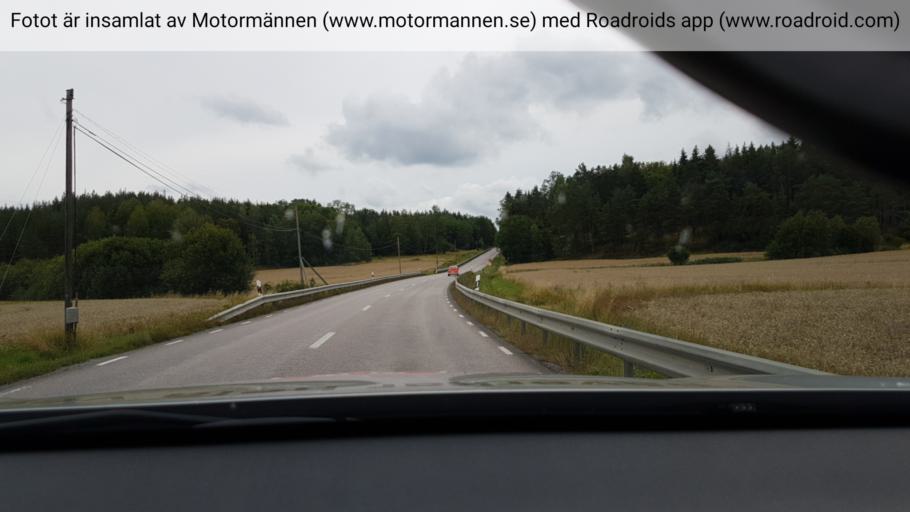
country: SE
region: Stockholm
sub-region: Sigtuna Kommun
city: Sigtuna
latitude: 59.6488
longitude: 17.7025
